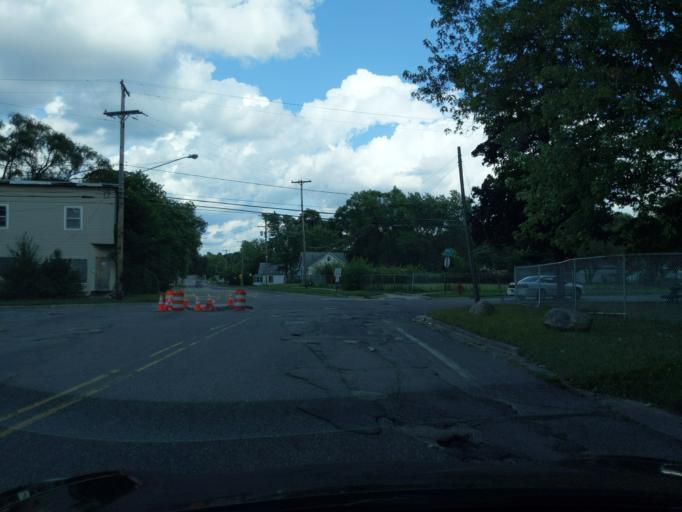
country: US
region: Michigan
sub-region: Jackson County
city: Jackson
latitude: 42.2651
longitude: -84.4123
